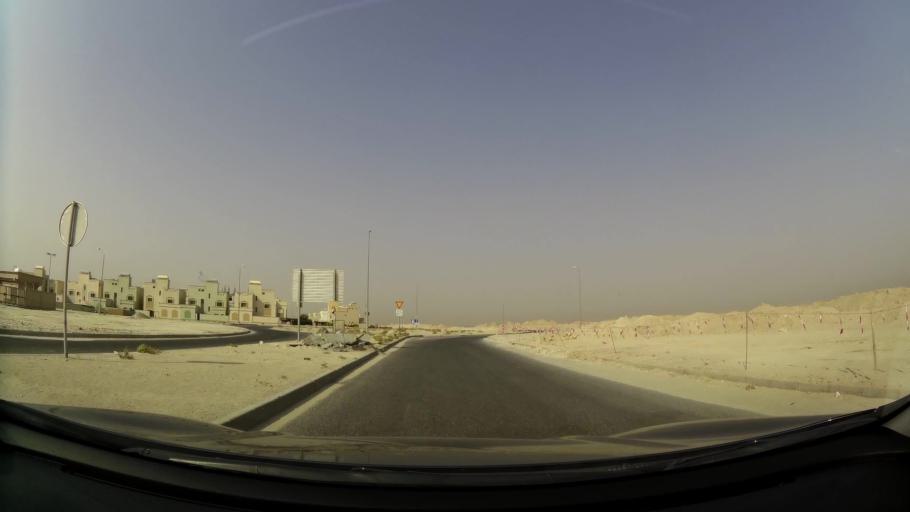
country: KW
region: Muhafazat al Jahra'
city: Al Jahra'
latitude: 29.3616
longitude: 47.7555
